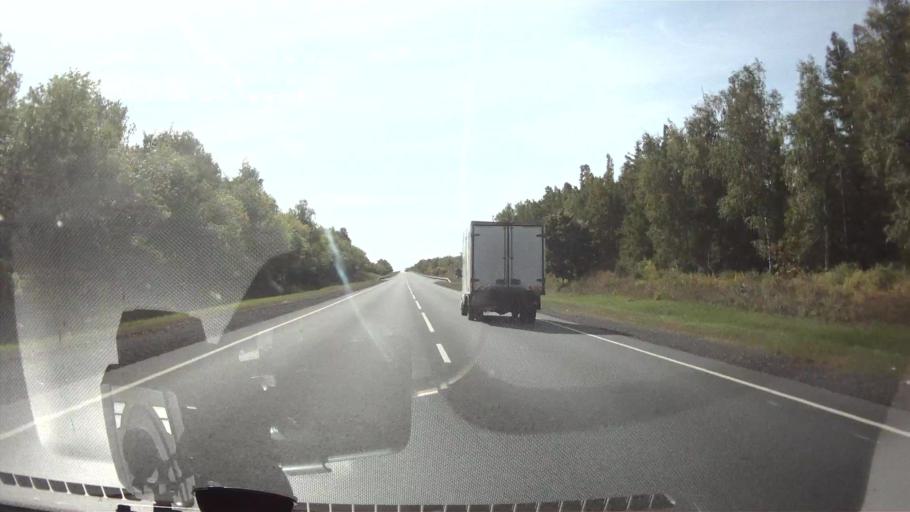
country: RU
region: Saratov
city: Khvalynsk
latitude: 52.5699
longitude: 48.1010
